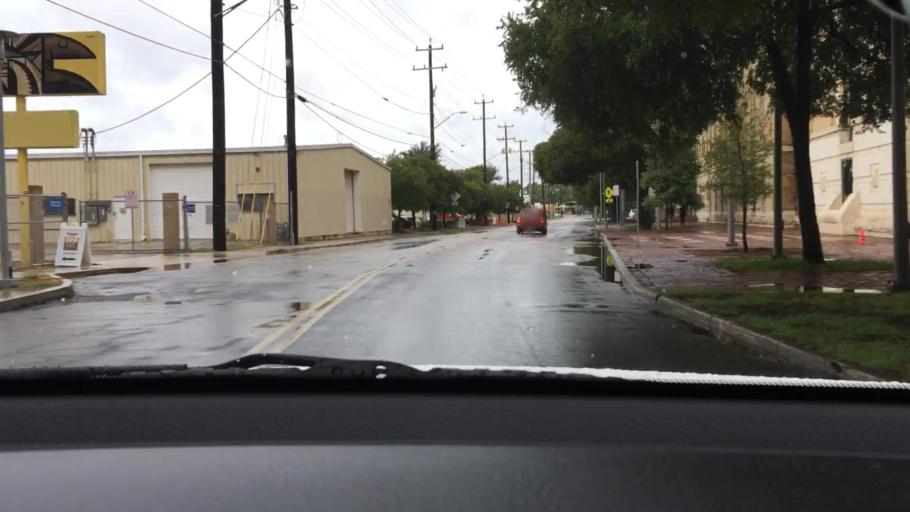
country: US
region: Texas
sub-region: Bexar County
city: San Antonio
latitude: 29.4366
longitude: -98.4815
